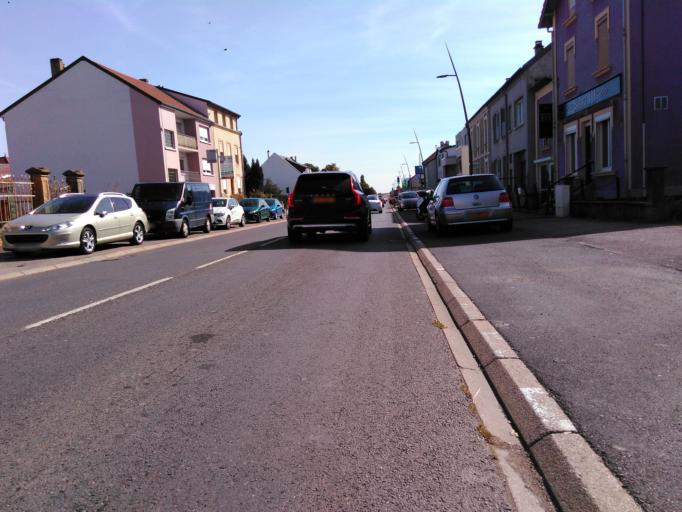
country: FR
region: Lorraine
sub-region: Departement de la Moselle
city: Hettange-Grande
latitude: 49.4025
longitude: 6.1584
